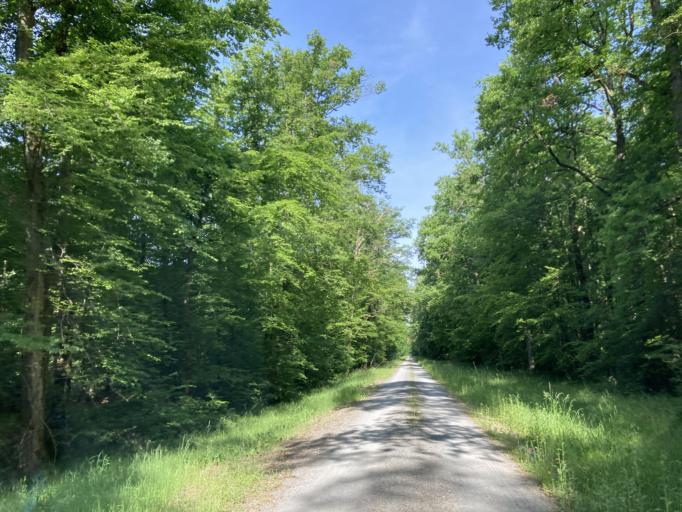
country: DE
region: Baden-Wuerttemberg
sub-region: Karlsruhe Region
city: Hambrucken
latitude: 49.2056
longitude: 8.5822
